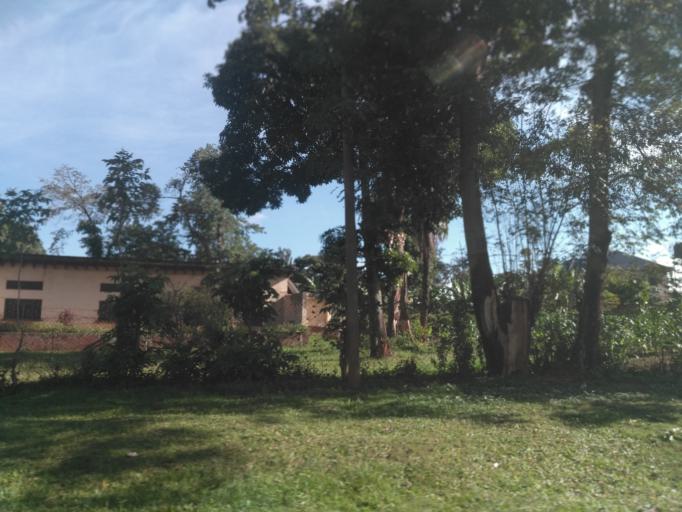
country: UG
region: Eastern Region
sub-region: Jinja District
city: Jinja
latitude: 0.4454
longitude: 33.1919
